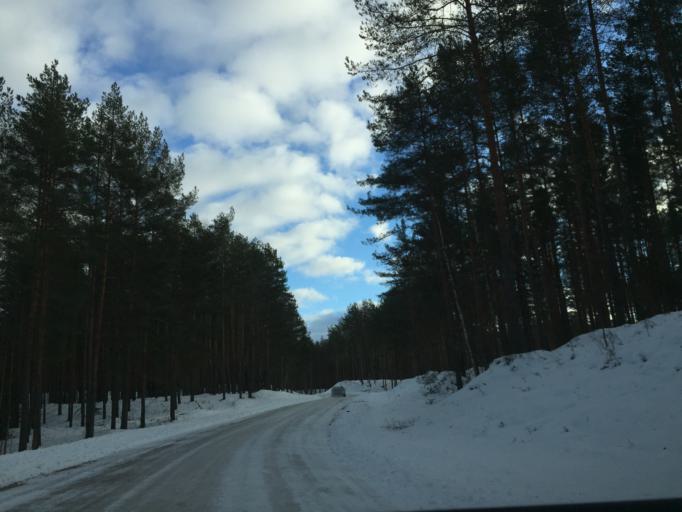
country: LV
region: Lielvarde
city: Lielvarde
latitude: 56.5616
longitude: 24.8423
